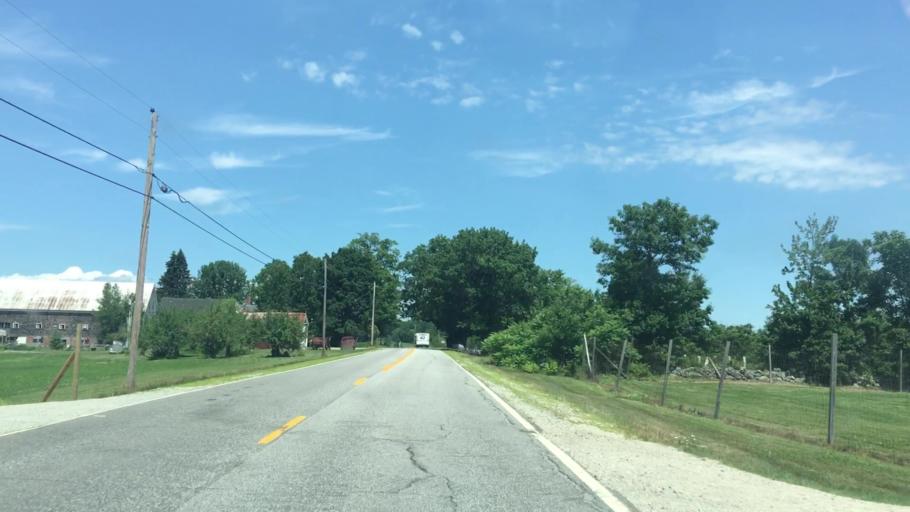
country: US
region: Maine
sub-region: Androscoggin County
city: Livermore
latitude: 44.3758
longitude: -70.2060
